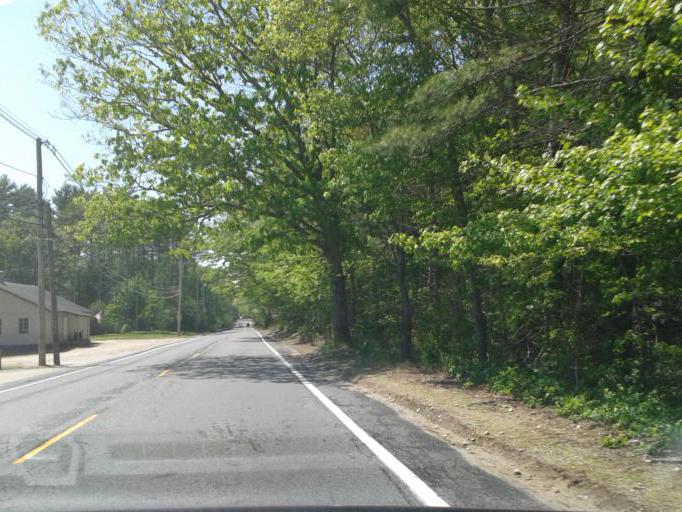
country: US
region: Rhode Island
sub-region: Washington County
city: Hope Valley
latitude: 41.5021
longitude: -71.6703
